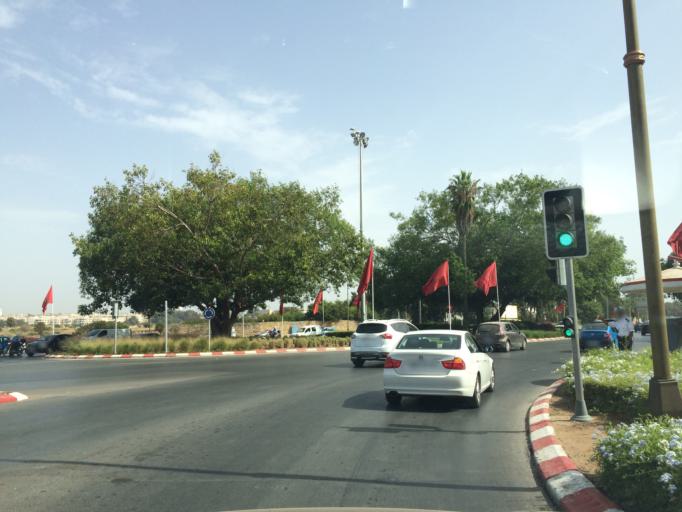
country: MA
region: Rabat-Sale-Zemmour-Zaer
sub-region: Rabat
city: Rabat
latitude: 34.0063
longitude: -6.8265
